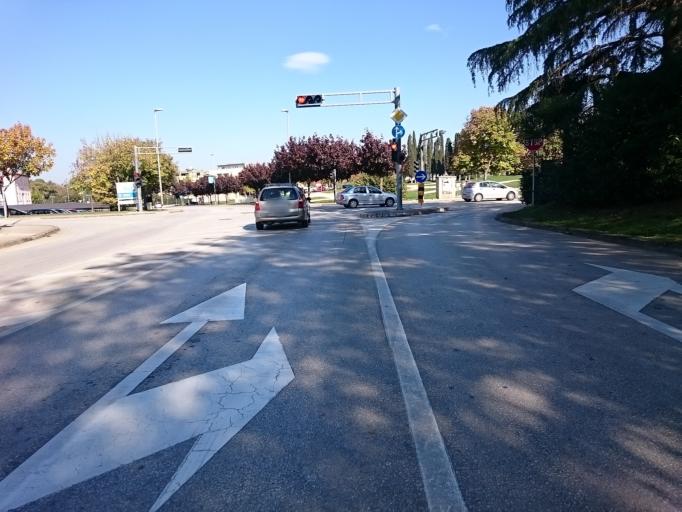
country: HR
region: Istarska
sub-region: Grad Porec
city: Porec
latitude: 45.2258
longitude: 13.6011
